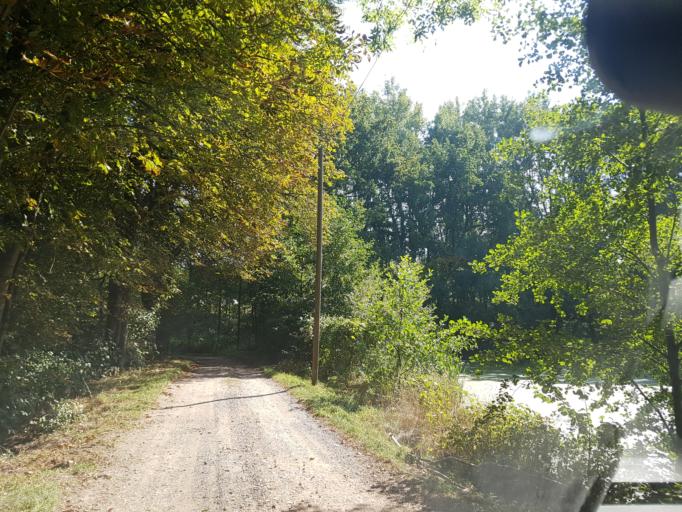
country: DE
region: Saxony
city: Kriebstein
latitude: 51.0437
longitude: 13.0066
